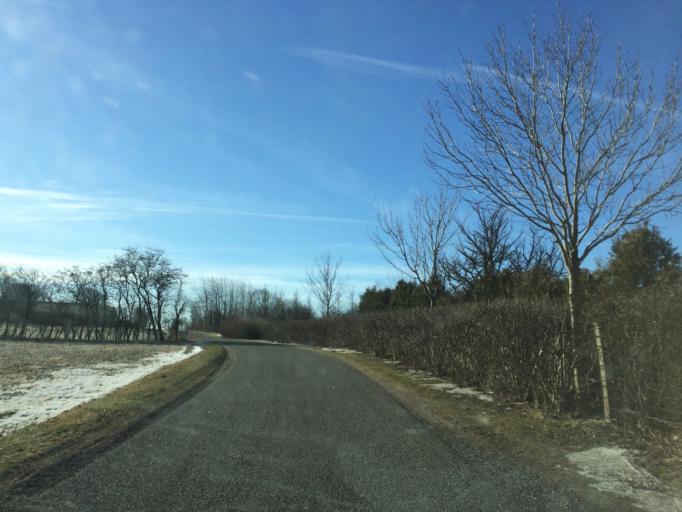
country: DK
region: North Denmark
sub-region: Mariagerfjord Kommune
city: Hobro
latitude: 56.6356
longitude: 9.6419
